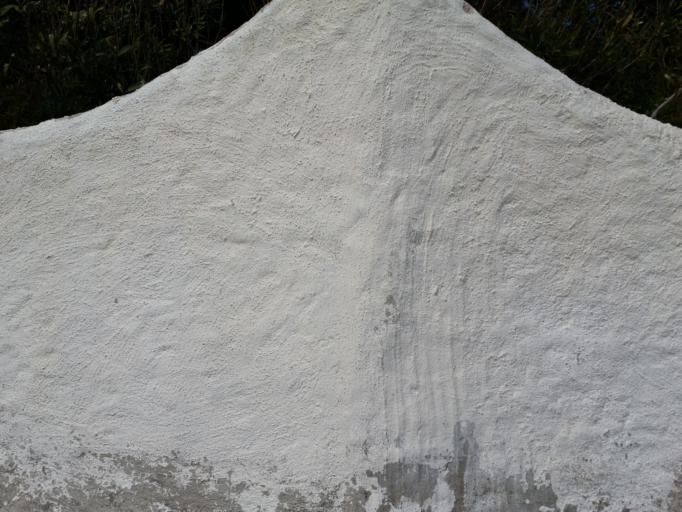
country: IT
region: Sardinia
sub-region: Provincia di Olbia-Tempio
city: Golfo Arnaci
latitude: 40.9468
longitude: 9.5738
